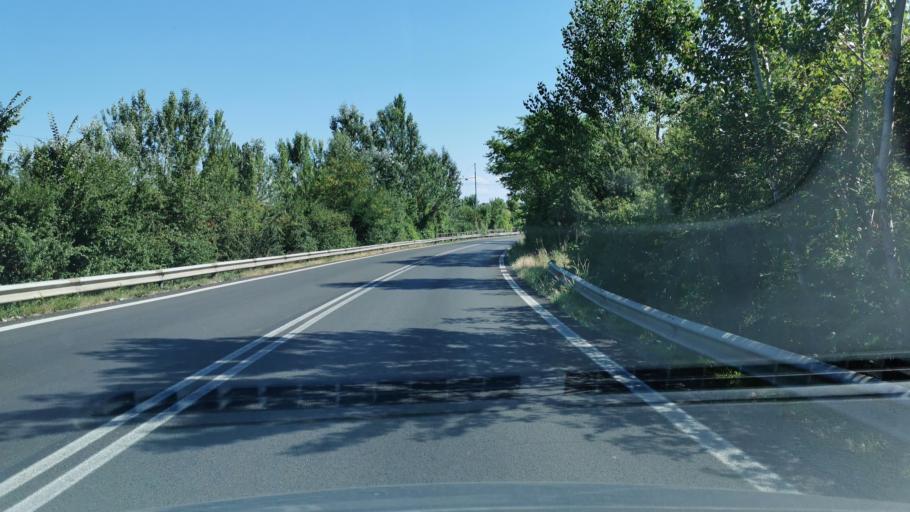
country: IT
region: Emilia-Romagna
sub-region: Provincia di Modena
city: Villanova
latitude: 44.6707
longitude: 10.9100
